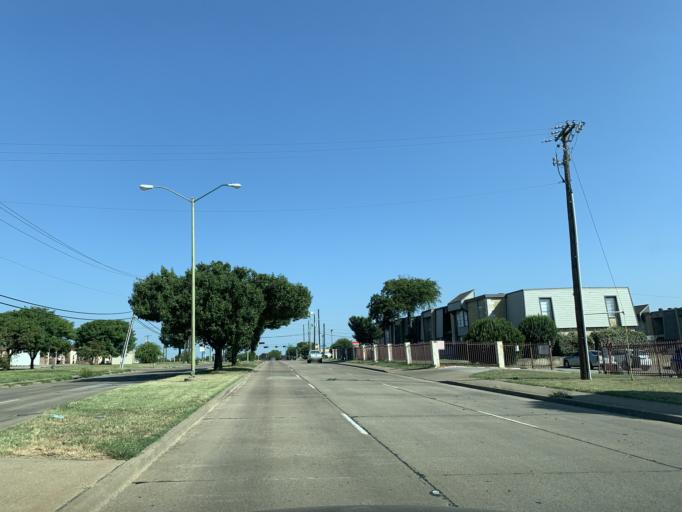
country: US
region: Texas
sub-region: Dallas County
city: Hutchins
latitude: 32.6711
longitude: -96.7617
